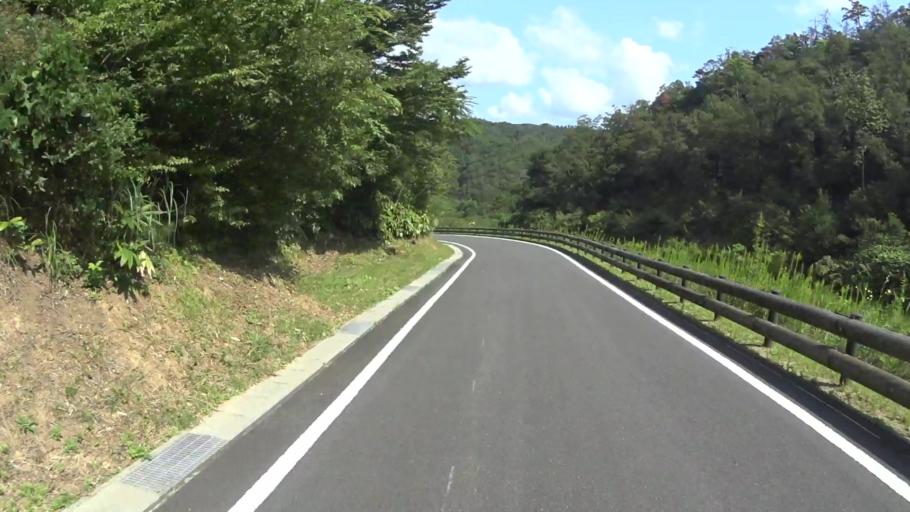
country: JP
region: Kyoto
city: Miyazu
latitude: 35.6237
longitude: 135.2343
